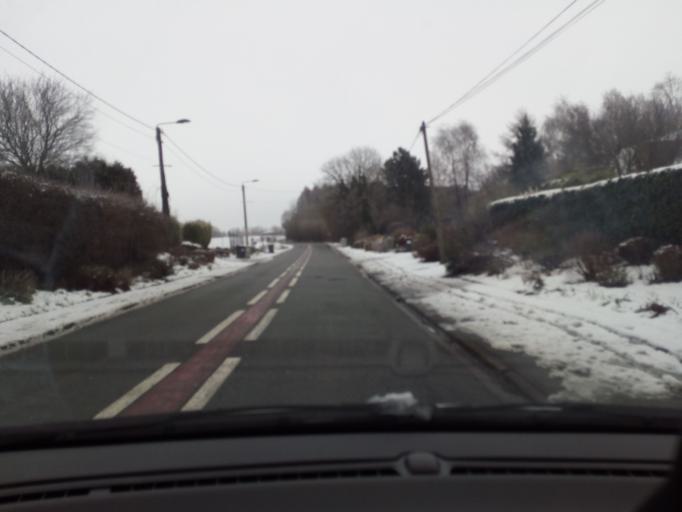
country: FR
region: Nord-Pas-de-Calais
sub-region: Departement du Nord
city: Maubeuge
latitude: 50.2905
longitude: 3.9879
